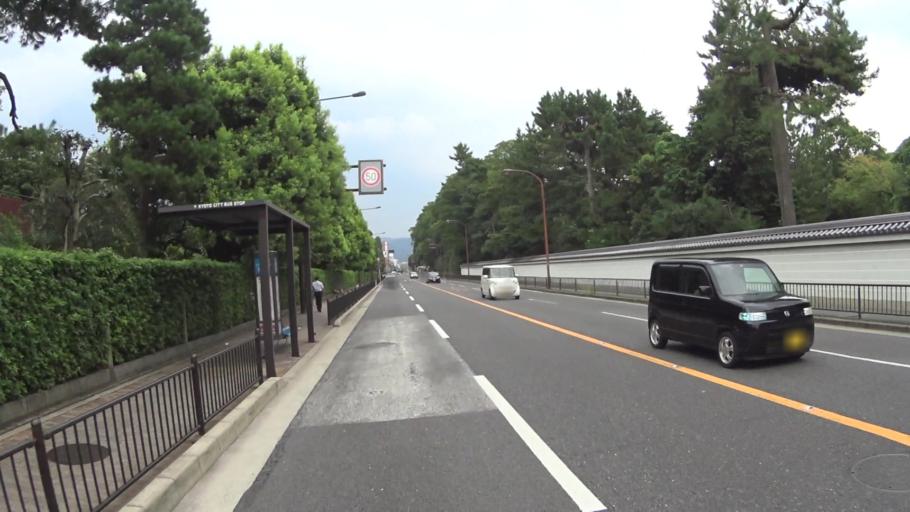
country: JP
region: Kyoto
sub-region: Kyoto-shi
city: Kamigyo-ku
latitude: 35.0292
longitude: 135.7631
